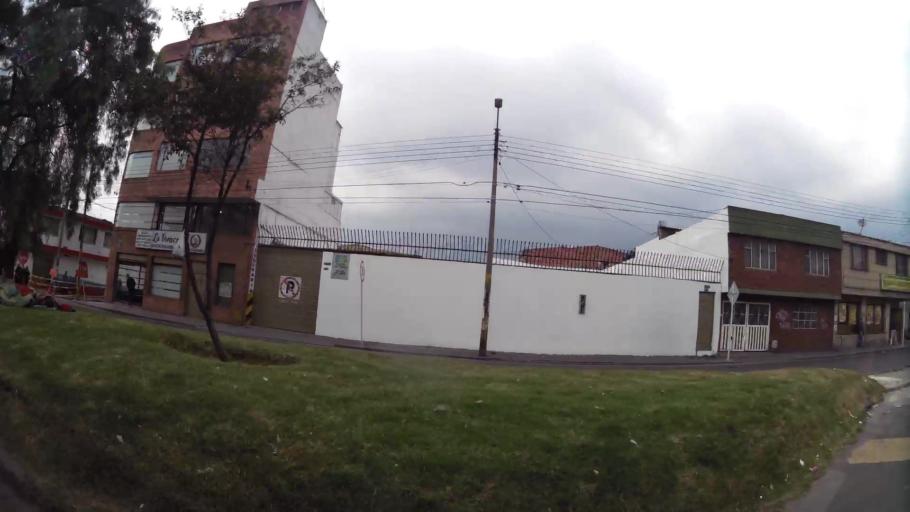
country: CO
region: Bogota D.C.
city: Bogota
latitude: 4.5761
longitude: -74.1031
